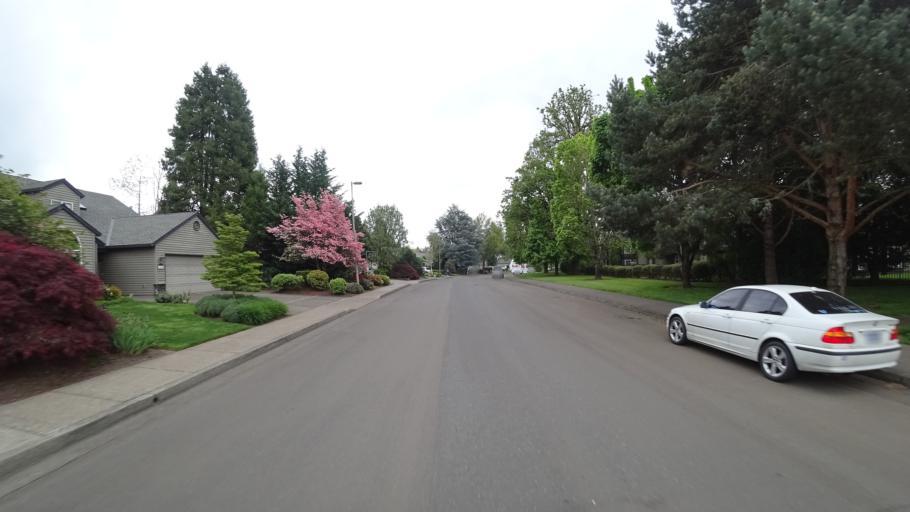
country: US
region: Oregon
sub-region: Washington County
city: Hillsboro
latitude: 45.5397
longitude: -122.9867
